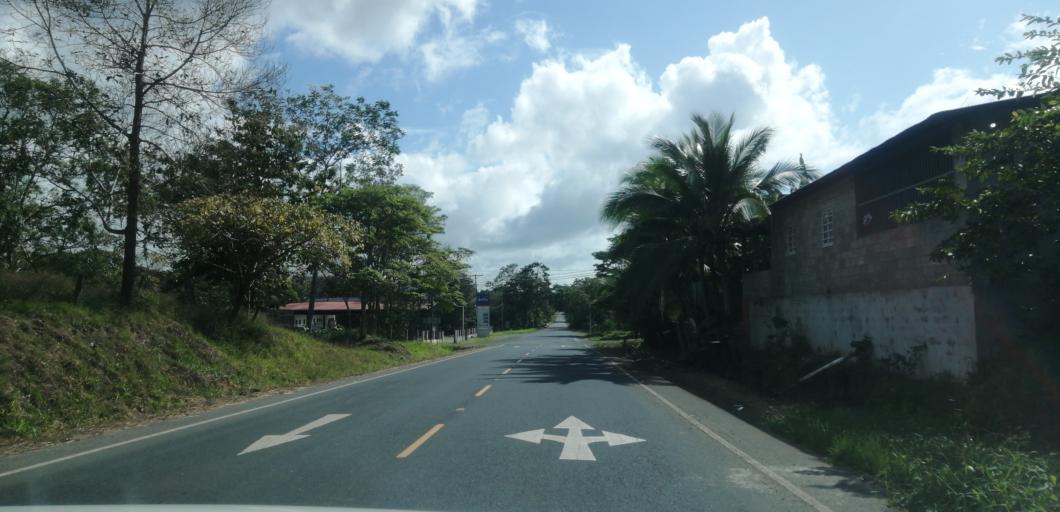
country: PA
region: Panama
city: Canita
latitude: 9.2214
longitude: -78.8901
